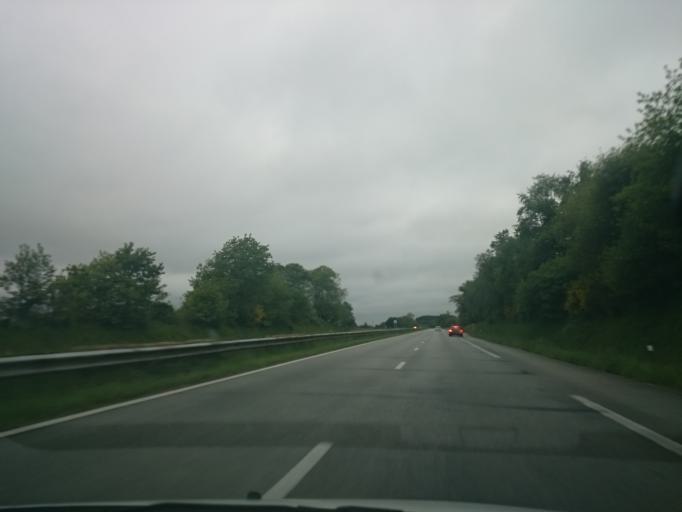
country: FR
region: Brittany
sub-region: Departement du Finistere
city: Saint-Yvi
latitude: 47.9610
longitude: -3.9608
